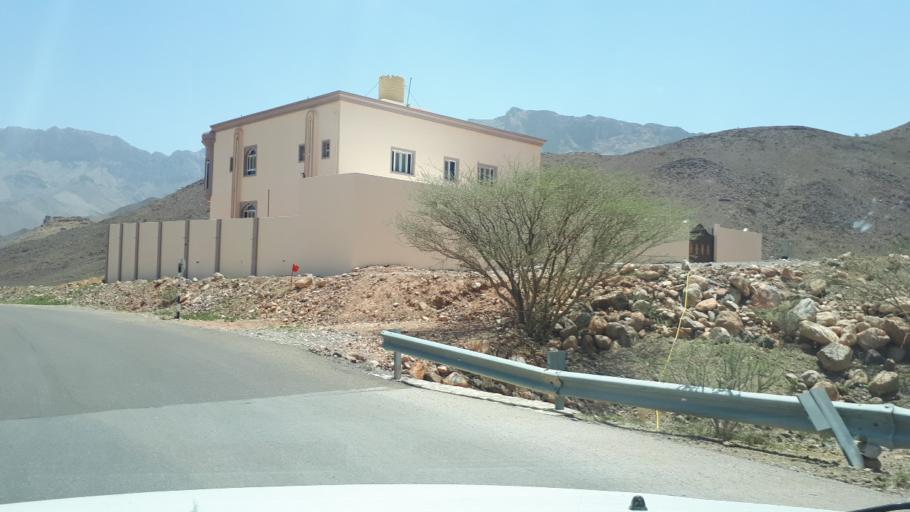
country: OM
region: Muhafazat ad Dakhiliyah
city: Bahla'
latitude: 23.1829
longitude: 57.1398
